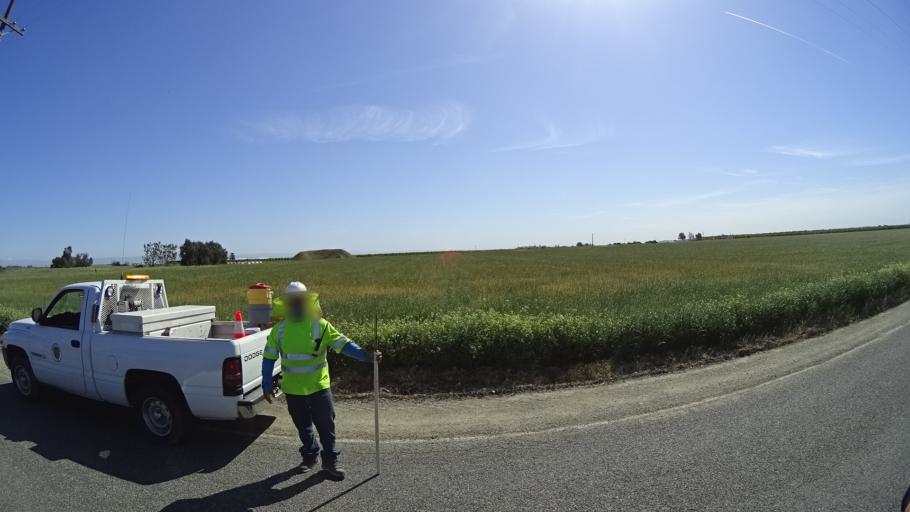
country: US
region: California
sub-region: Glenn County
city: Orland
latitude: 39.6494
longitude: -122.1786
